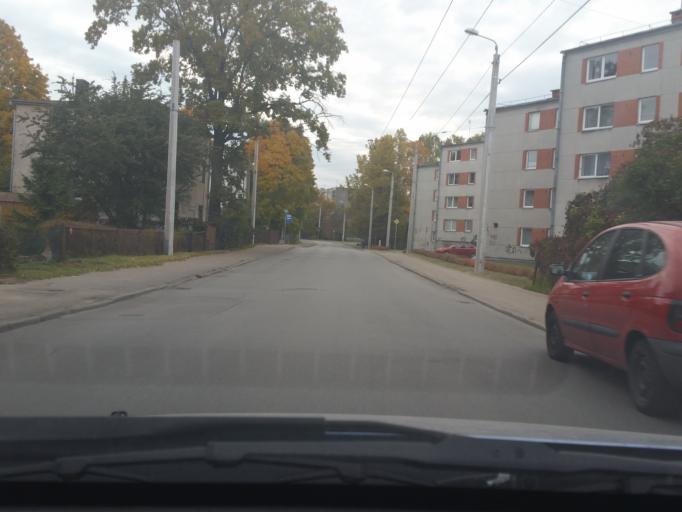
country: LV
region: Riga
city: Jaunciems
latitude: 56.9740
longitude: 24.1812
